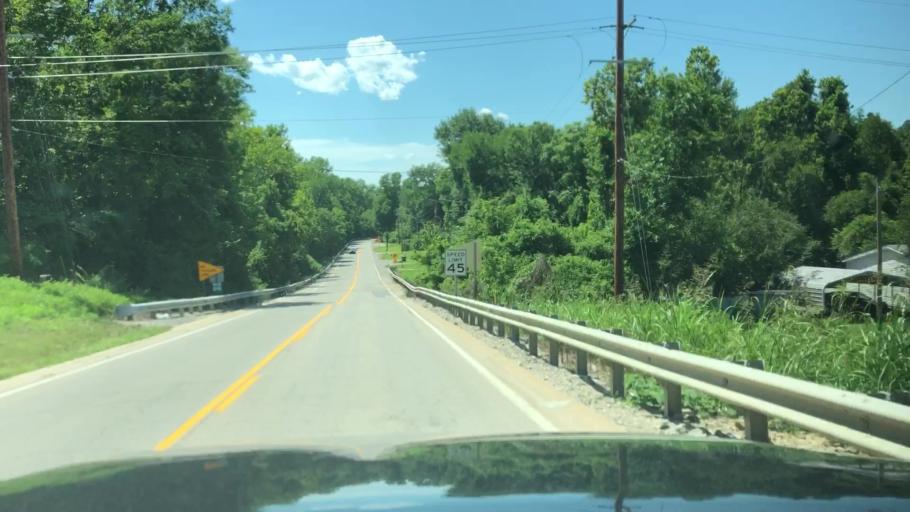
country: US
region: Illinois
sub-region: Saint Clair County
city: Centreville
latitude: 38.5538
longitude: -90.0907
